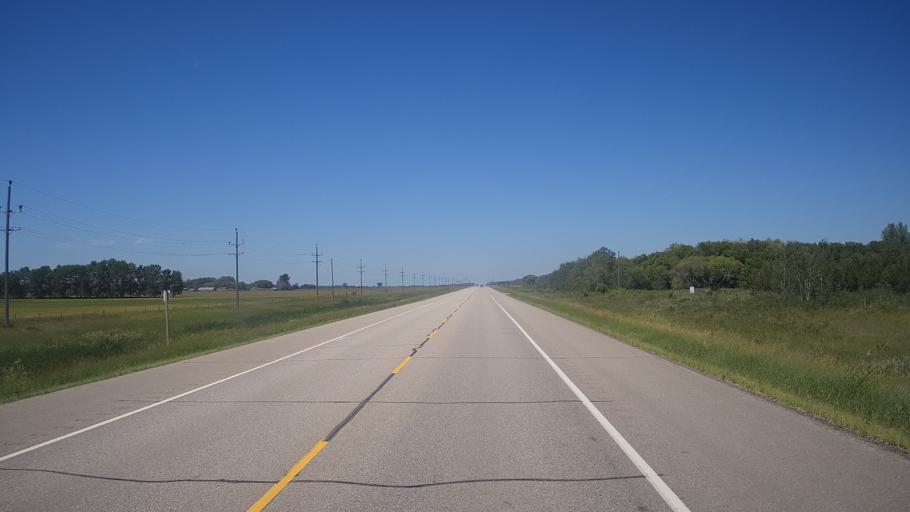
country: CA
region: Manitoba
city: Neepawa
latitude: 50.2257
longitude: -99.0504
